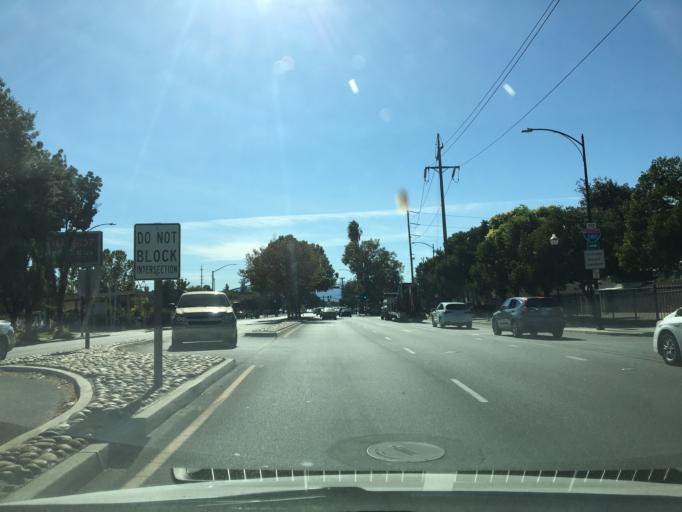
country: US
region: California
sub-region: Santa Clara County
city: San Jose
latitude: 37.3253
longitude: -121.8665
